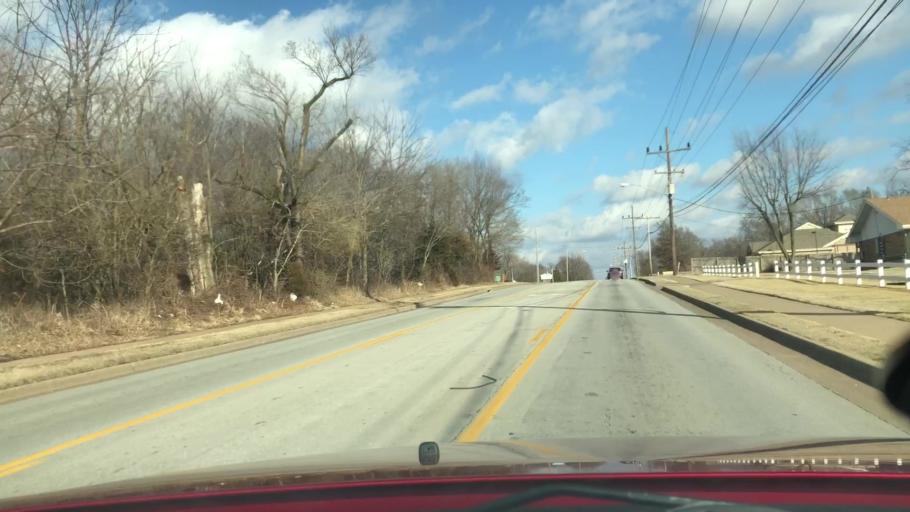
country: US
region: Missouri
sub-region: Greene County
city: Springfield
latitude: 37.2516
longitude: -93.2890
